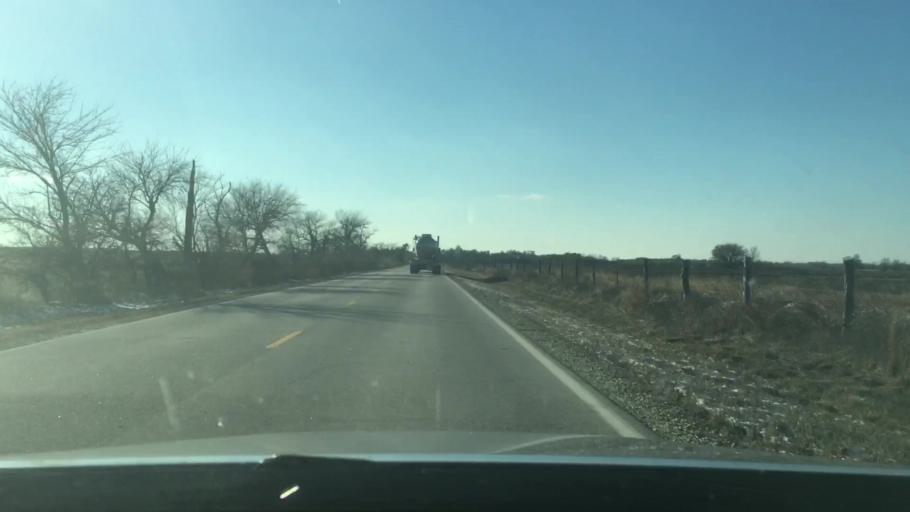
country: US
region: Kansas
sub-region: Reno County
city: Nickerson
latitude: 38.1448
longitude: -98.1252
